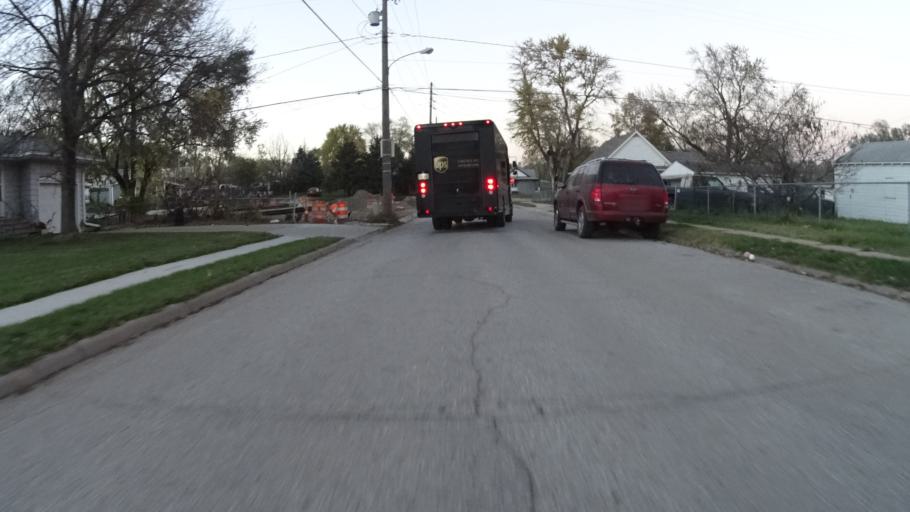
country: US
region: Nebraska
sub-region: Douglas County
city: Omaha
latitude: 41.1939
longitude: -95.9456
